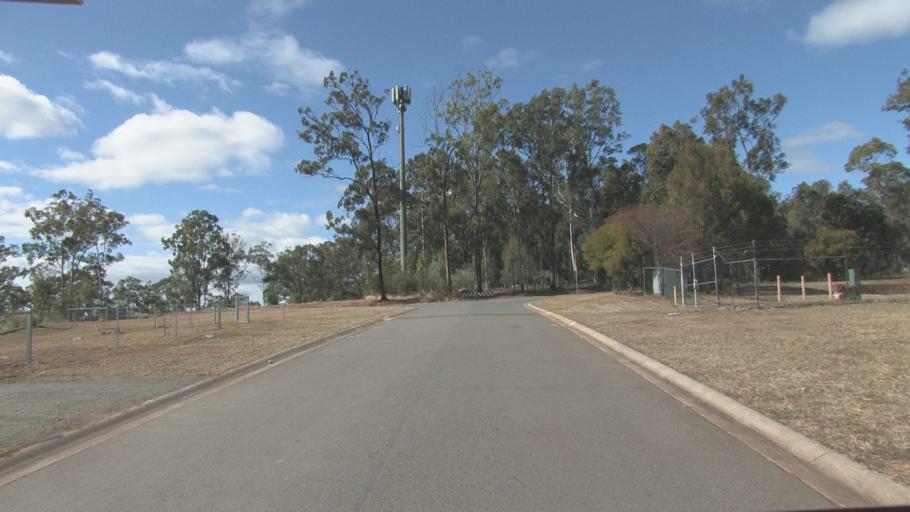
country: AU
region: Queensland
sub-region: Logan
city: Cedar Vale
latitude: -27.8922
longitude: 153.0016
